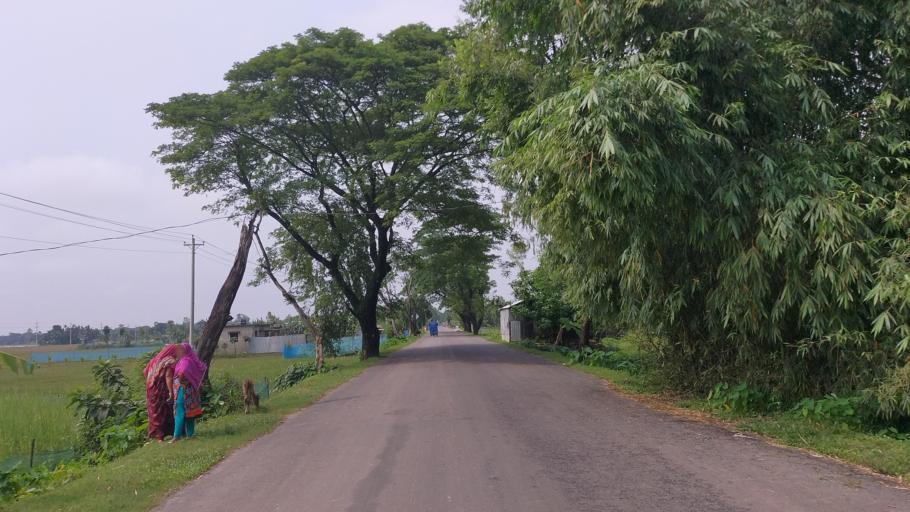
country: BD
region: Dhaka
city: Netrakona
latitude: 24.9470
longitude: 90.8315
